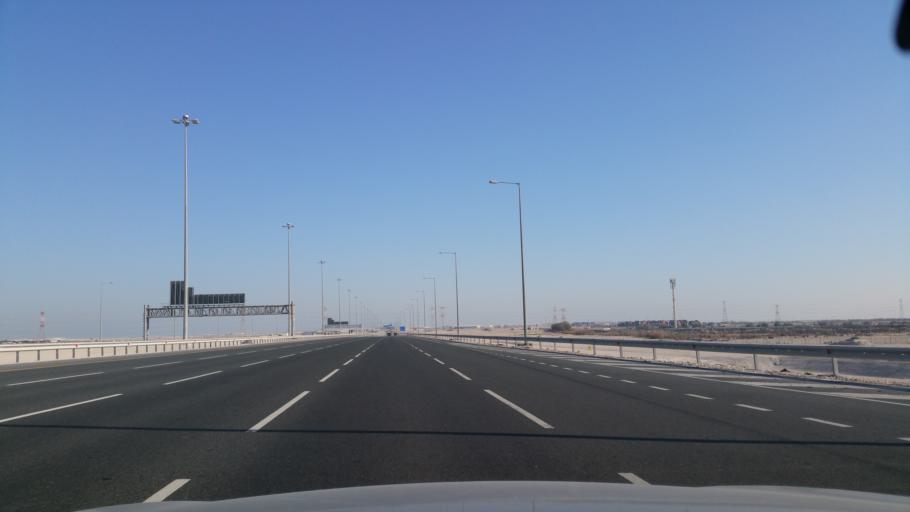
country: QA
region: Al Wakrah
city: Al Wukayr
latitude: 25.1143
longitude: 51.4953
